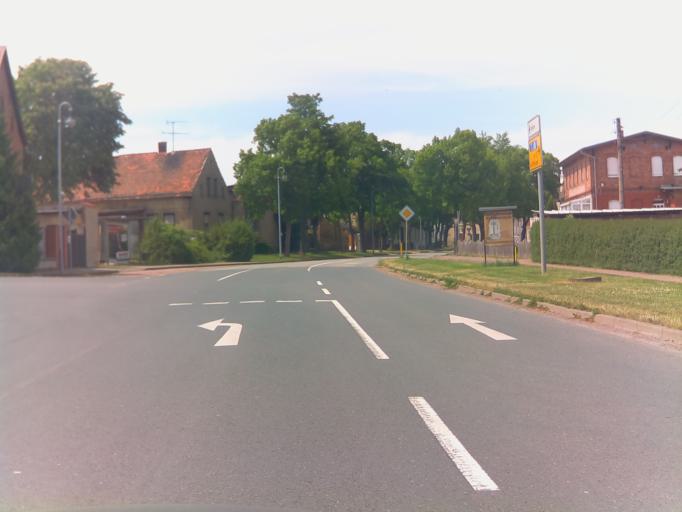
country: DE
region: Saxony-Anhalt
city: Kroppenstedt
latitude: 51.9404
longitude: 11.3163
